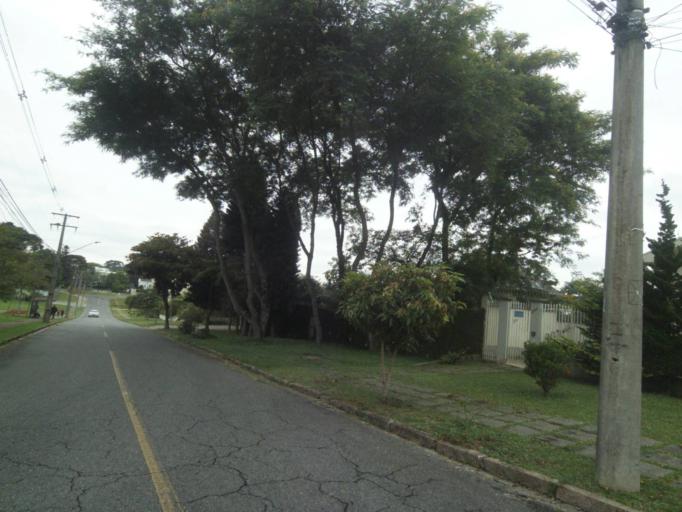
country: BR
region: Parana
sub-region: Curitiba
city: Curitiba
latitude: -25.4073
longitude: -49.2862
